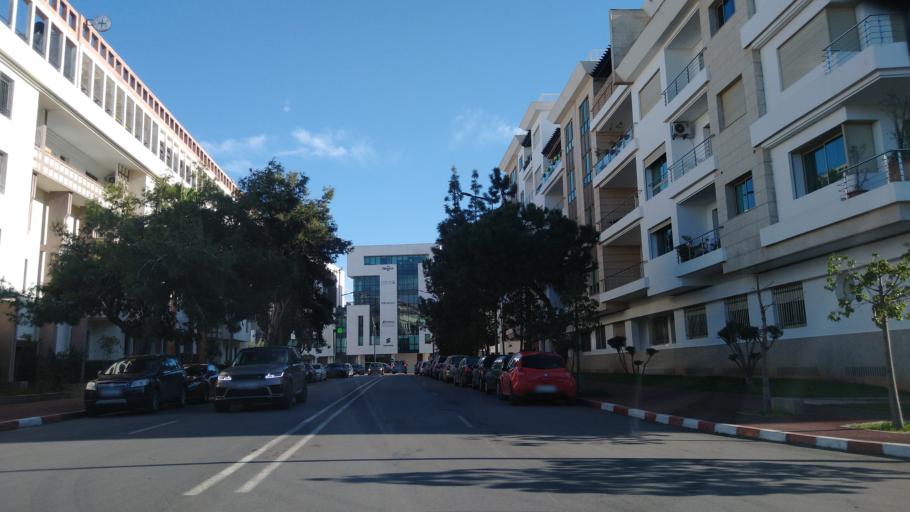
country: MA
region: Rabat-Sale-Zemmour-Zaer
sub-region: Skhirate-Temara
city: Temara
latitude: 33.9632
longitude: -6.8676
